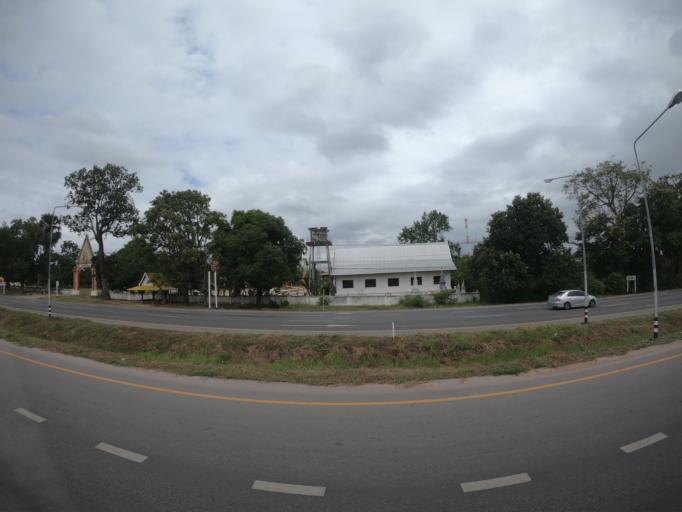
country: TH
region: Maha Sarakham
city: Kut Rang
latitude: 16.0470
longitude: 102.9075
